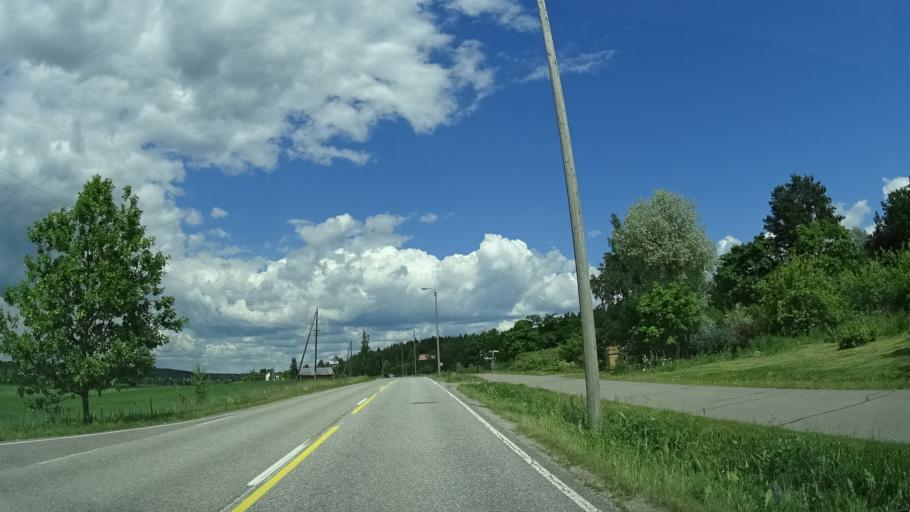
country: FI
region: Uusimaa
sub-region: Helsinki
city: Nurmijaervi
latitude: 60.3905
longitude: 24.6434
